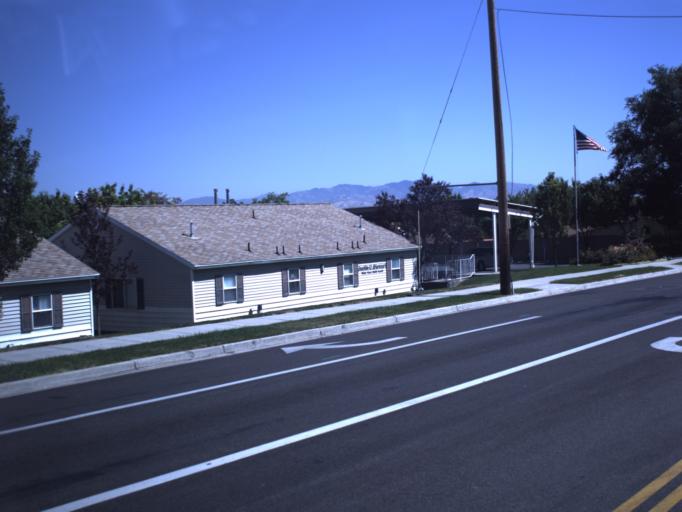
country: US
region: Utah
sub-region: Salt Lake County
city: Magna
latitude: 40.6965
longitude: -112.0819
